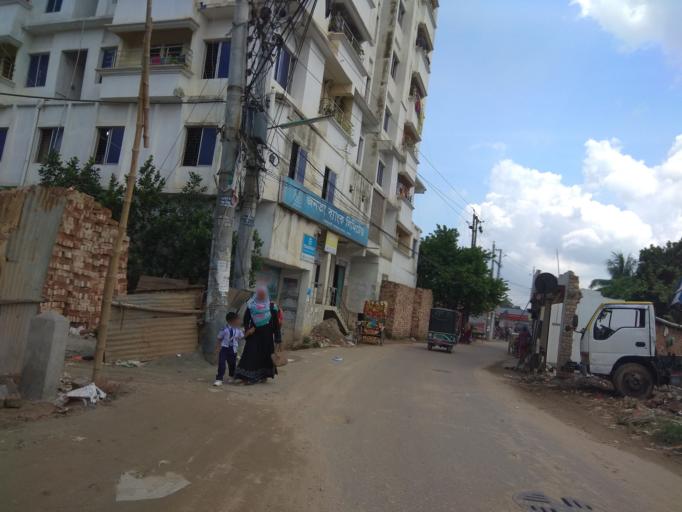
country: BD
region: Dhaka
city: Tungi
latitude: 23.8321
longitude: 90.3889
